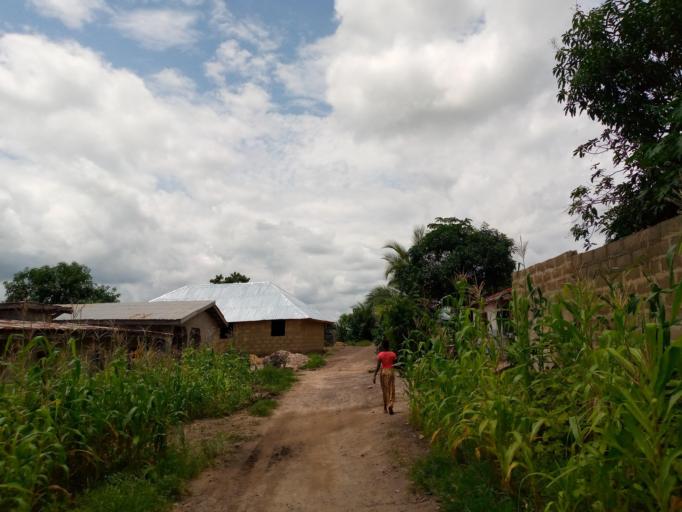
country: SL
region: Northern Province
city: Magburaka
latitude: 8.7303
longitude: -11.9391
